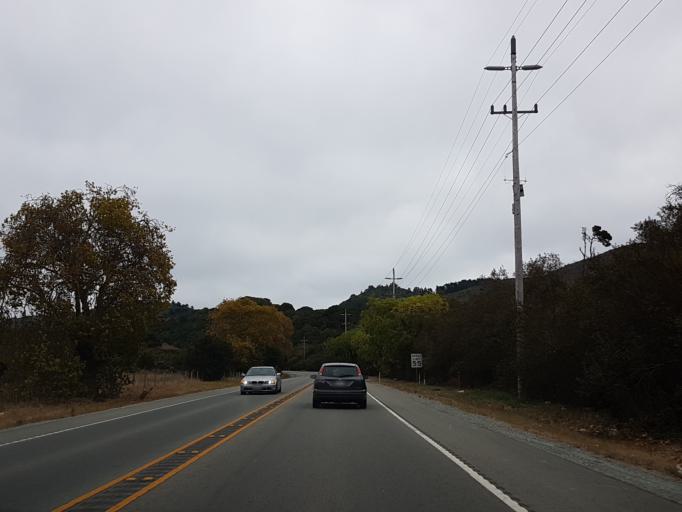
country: US
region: California
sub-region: Monterey County
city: Del Rey Oaks
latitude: 36.5750
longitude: -121.8221
